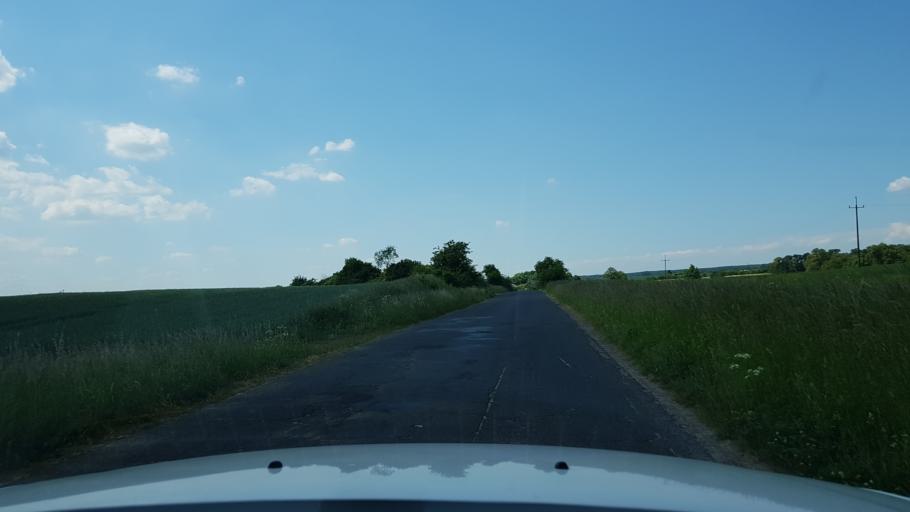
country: PL
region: West Pomeranian Voivodeship
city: Trzcinsko Zdroj
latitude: 52.9949
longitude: 14.5789
